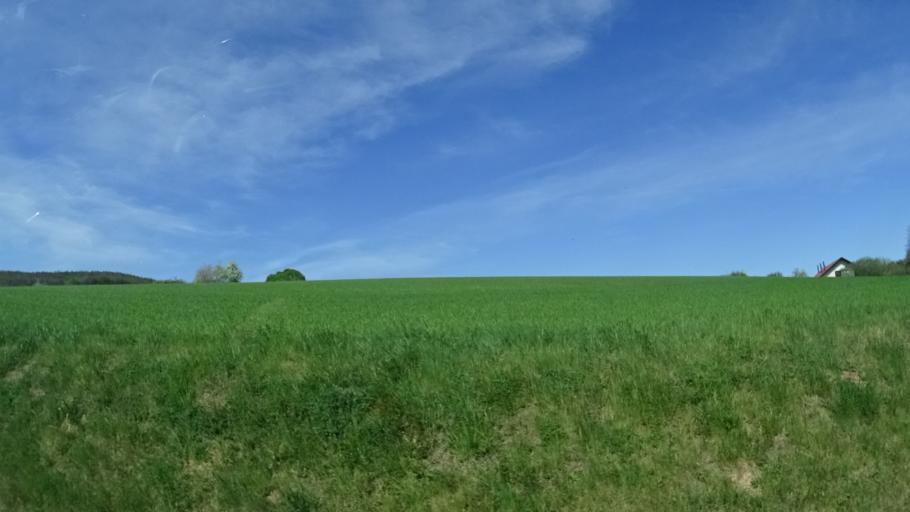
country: DE
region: Bavaria
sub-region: Regierungsbezirk Unterfranken
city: Burgpreppach
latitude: 50.1527
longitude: 10.6305
